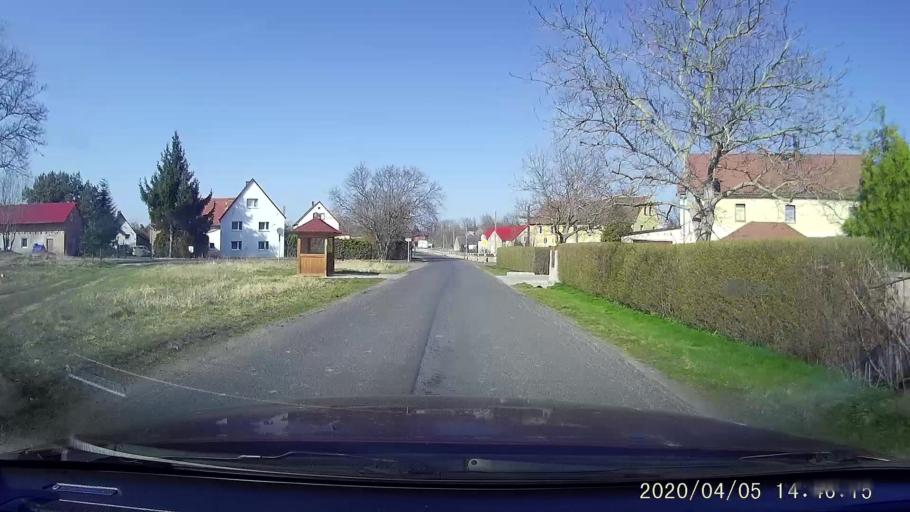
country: PL
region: Lower Silesian Voivodeship
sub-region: Powiat zgorzelecki
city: Sulikow
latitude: 51.0564
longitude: 15.1086
